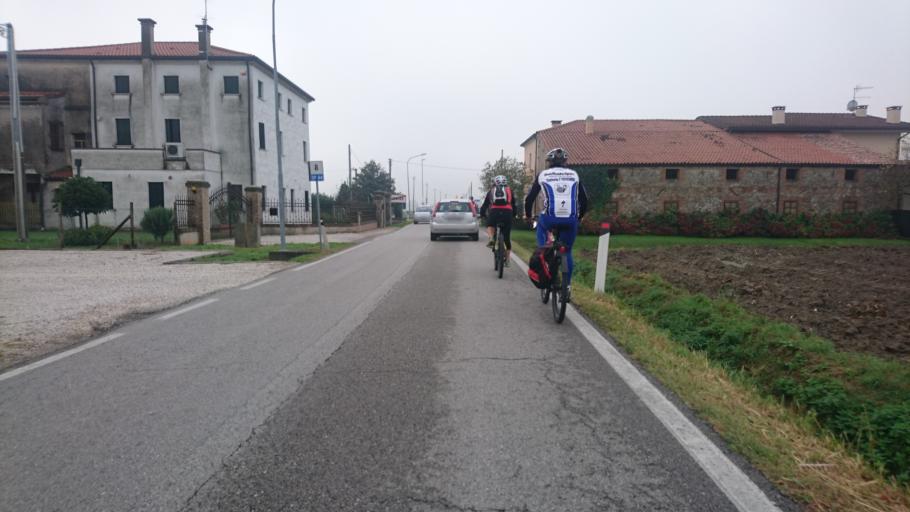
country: IT
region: Veneto
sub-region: Provincia di Padova
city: Pozzonovo
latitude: 45.1856
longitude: 11.7892
